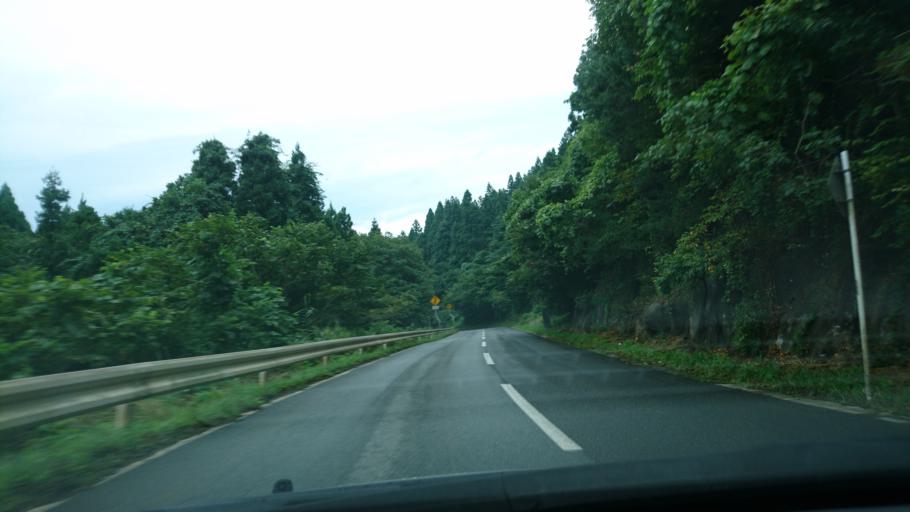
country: JP
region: Iwate
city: Mizusawa
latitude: 39.0382
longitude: 141.1918
